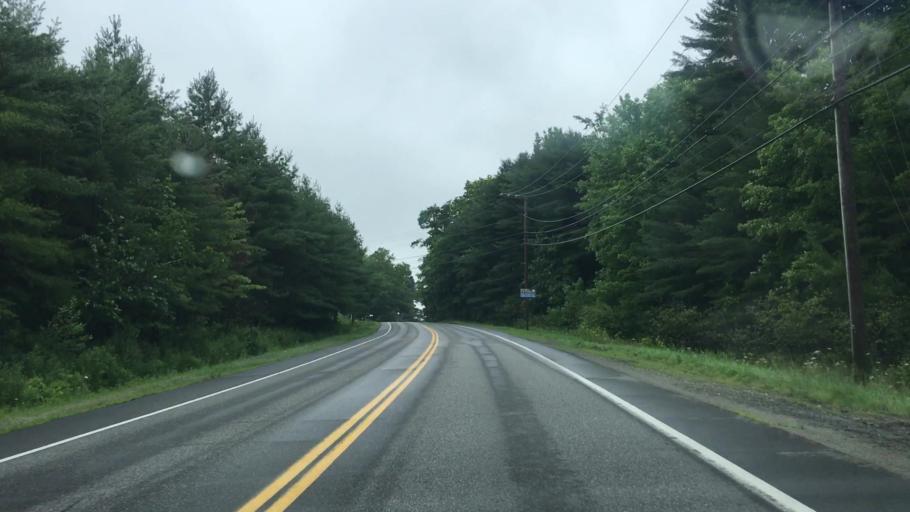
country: US
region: Maine
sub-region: Kennebec County
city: Augusta
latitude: 44.3410
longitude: -69.8094
